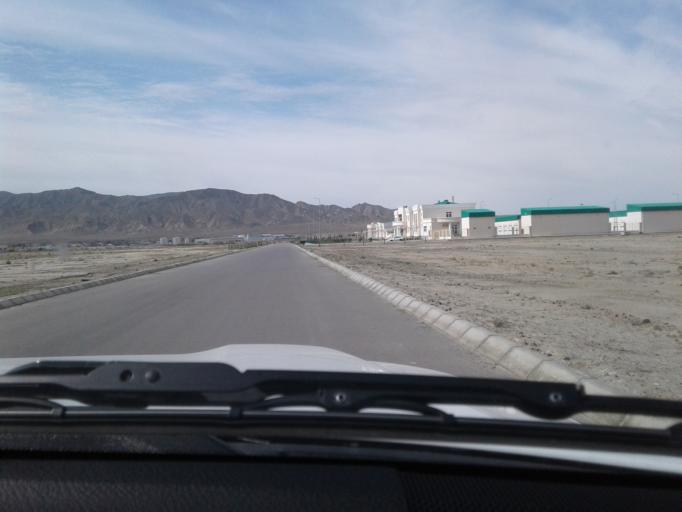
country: TM
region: Balkan
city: Gazanjyk
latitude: 39.2656
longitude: 55.4910
